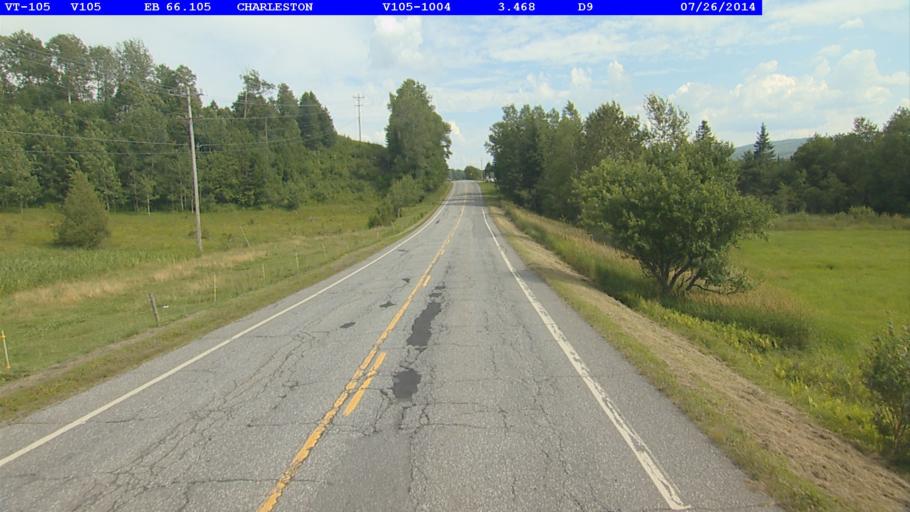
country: US
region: Vermont
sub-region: Orleans County
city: Newport
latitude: 44.8673
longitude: -72.0462
